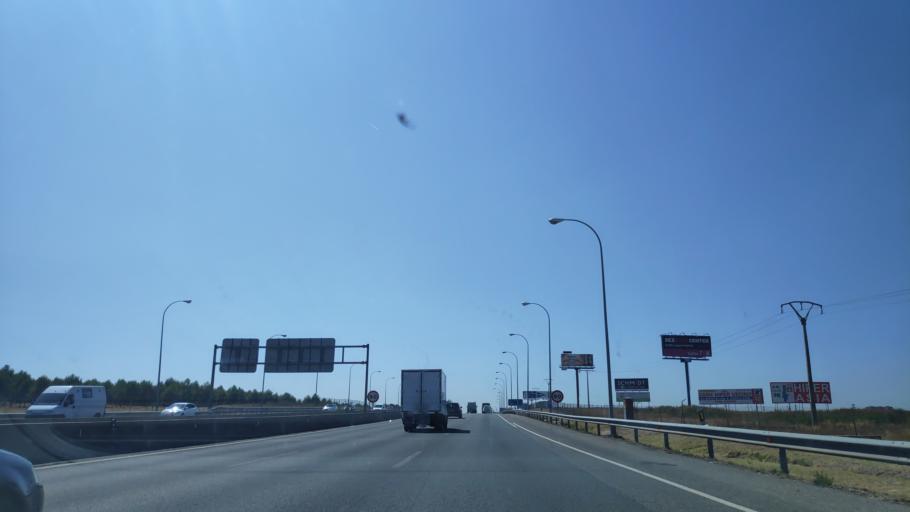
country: ES
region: Madrid
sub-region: Provincia de Madrid
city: Villaverde
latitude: 40.3583
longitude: -3.7217
